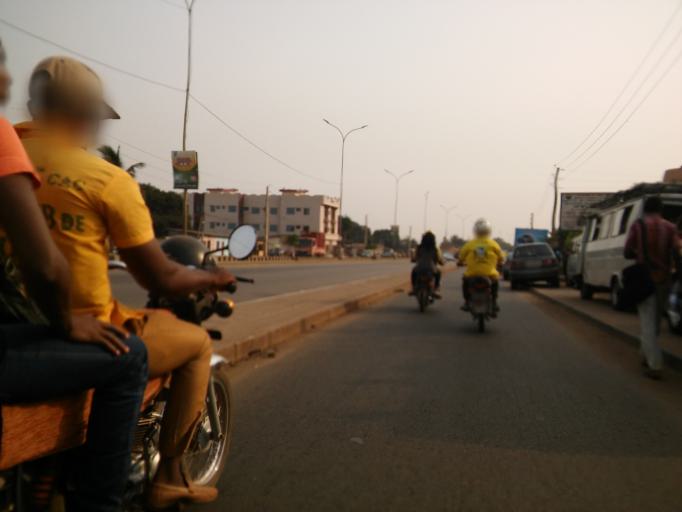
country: BJ
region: Atlantique
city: Abomey-Calavi
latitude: 6.4122
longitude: 2.3449
